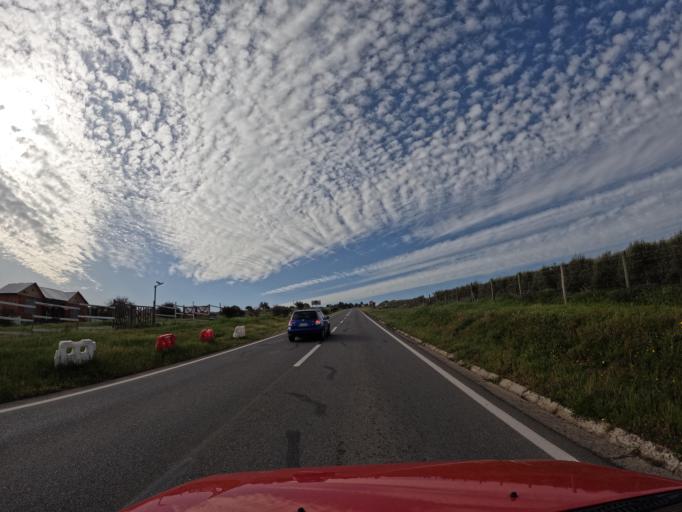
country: CL
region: O'Higgins
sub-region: Provincia de Colchagua
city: Santa Cruz
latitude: -34.2743
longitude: -71.7310
